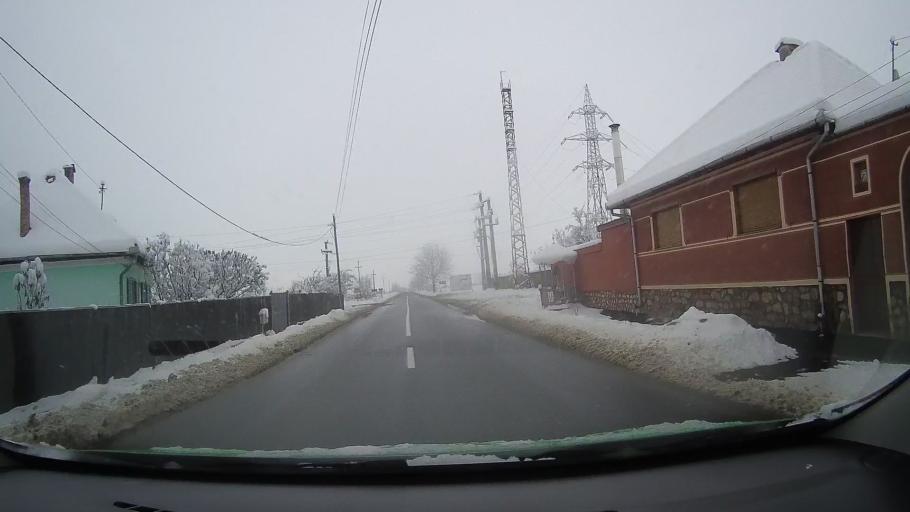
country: RO
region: Sibiu
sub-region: Comuna Orlat
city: Orlat
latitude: 45.7594
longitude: 23.9787
